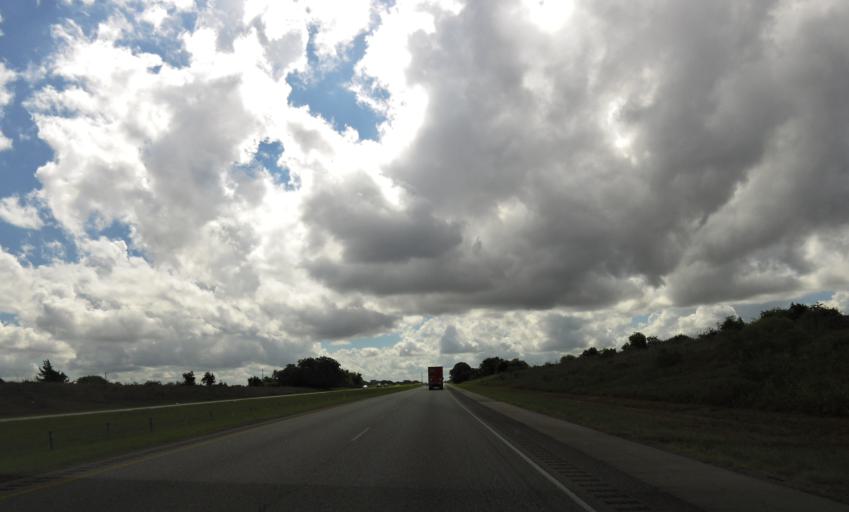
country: US
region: Texas
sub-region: Fayette County
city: Flatonia
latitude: 29.6964
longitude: -97.0363
